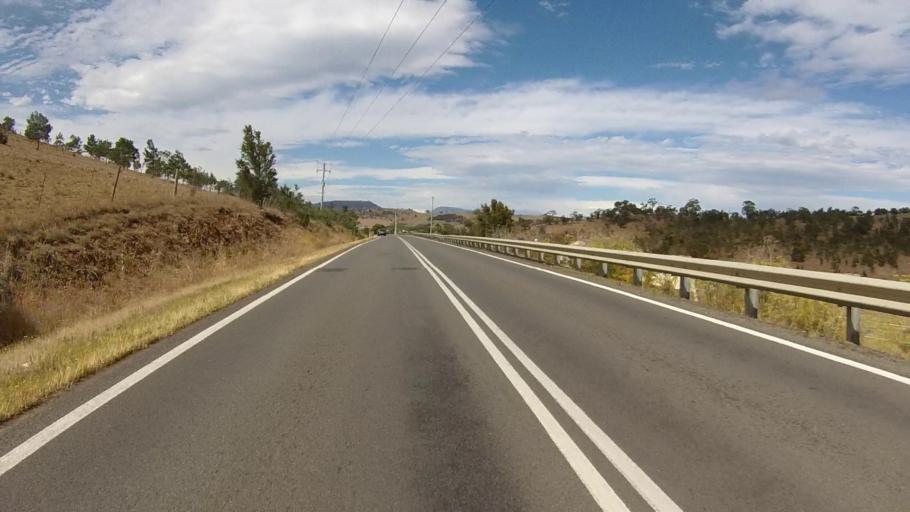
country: AU
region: Tasmania
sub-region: Brighton
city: Old Beach
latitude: -42.6797
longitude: 147.3541
